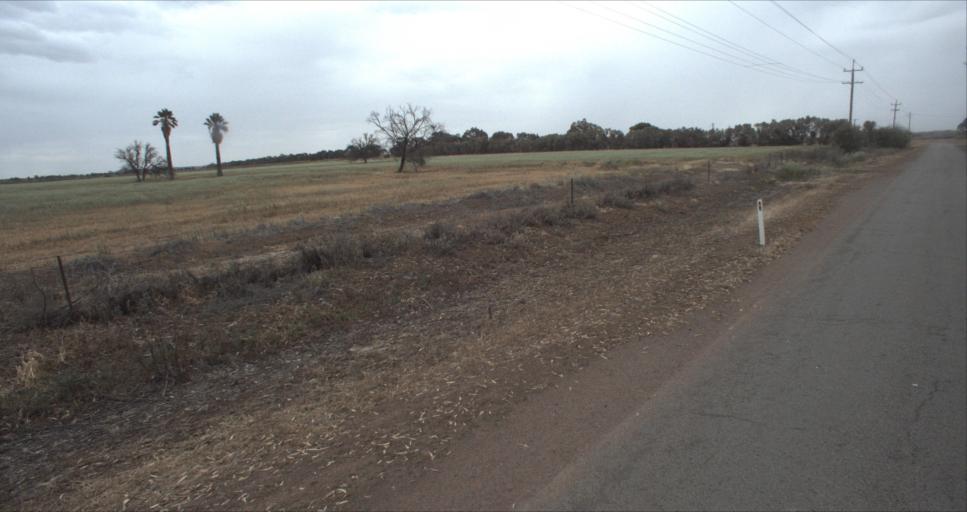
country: AU
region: New South Wales
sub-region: Leeton
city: Leeton
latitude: -34.4056
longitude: 146.3413
